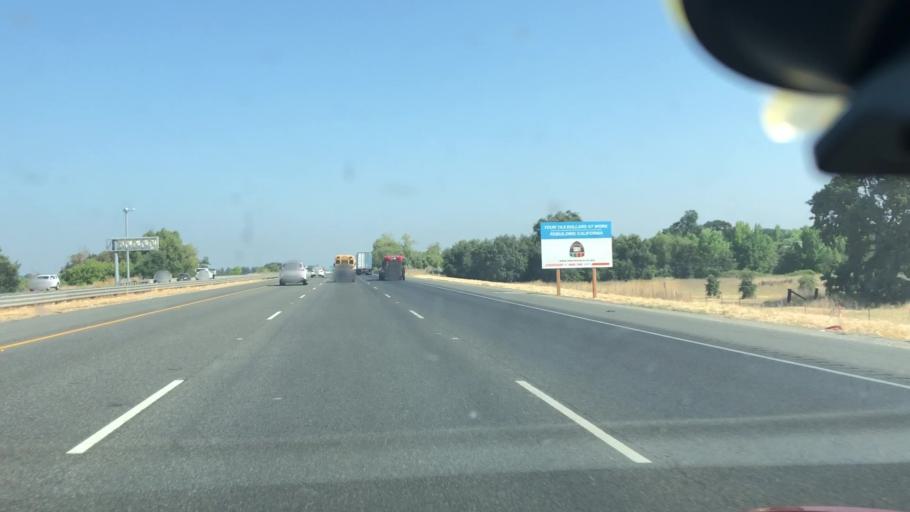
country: US
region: California
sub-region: Sacramento County
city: Parkway
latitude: 38.4373
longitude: -121.4895
